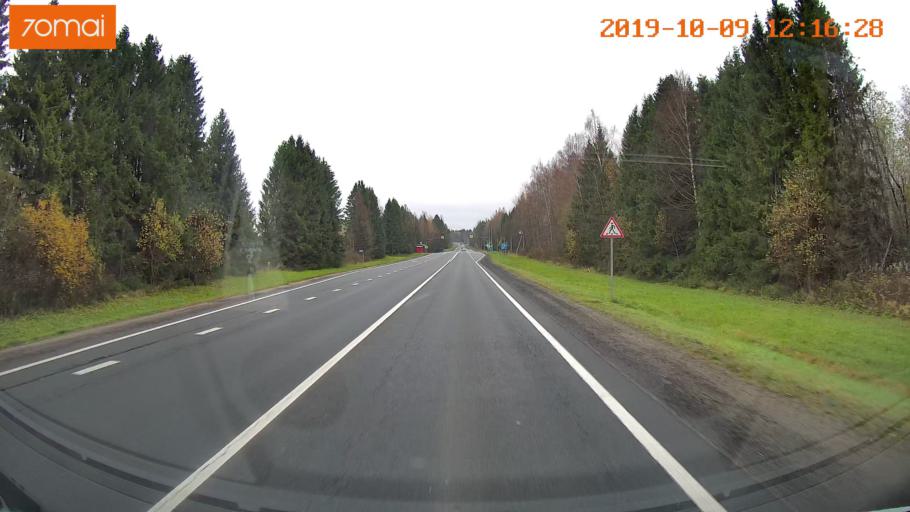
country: RU
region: Jaroslavl
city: Prechistoye
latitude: 58.4681
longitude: 40.3211
